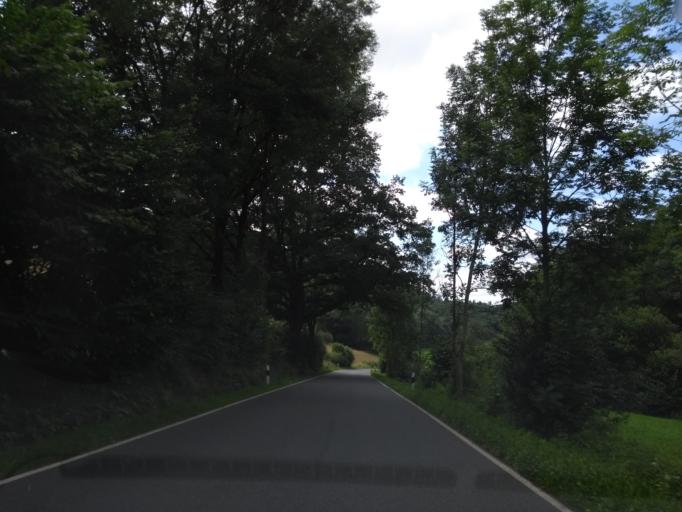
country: DE
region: North Rhine-Westphalia
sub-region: Regierungsbezirk Detmold
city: Lugde
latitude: 51.9499
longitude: 9.2701
